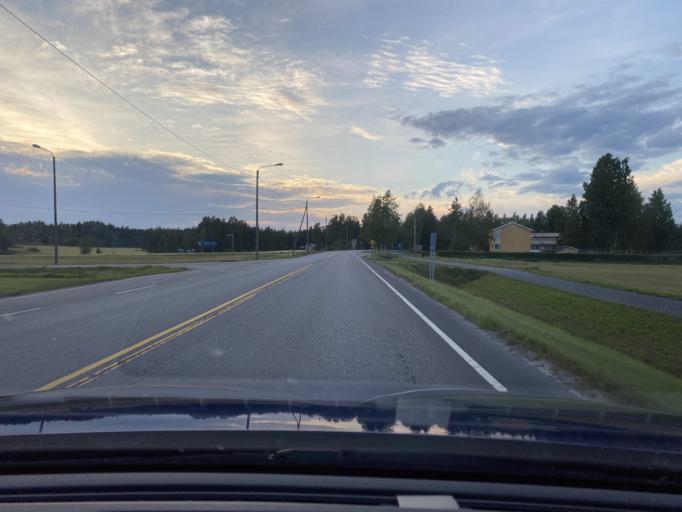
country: FI
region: Satakunta
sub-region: Pohjois-Satakunta
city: Kankaanpaeae
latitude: 61.7544
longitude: 22.5081
